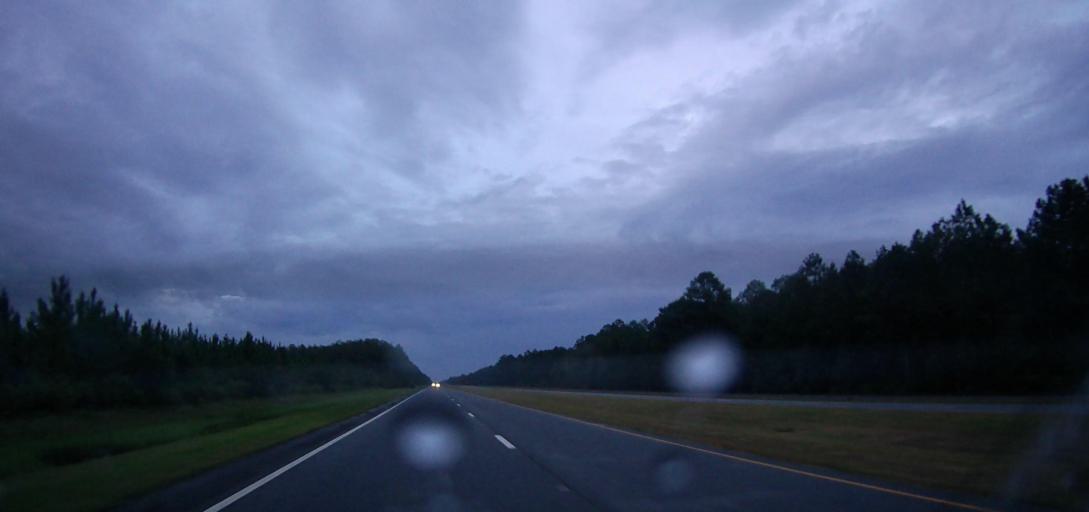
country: US
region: Georgia
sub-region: Lowndes County
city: Valdosta
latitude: 30.8750
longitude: -83.1641
